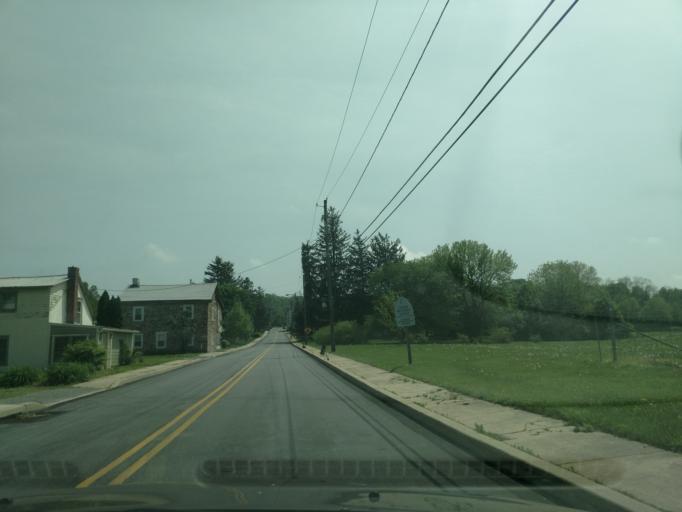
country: US
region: Pennsylvania
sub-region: Chester County
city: Elverson
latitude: 40.1593
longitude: -75.8334
